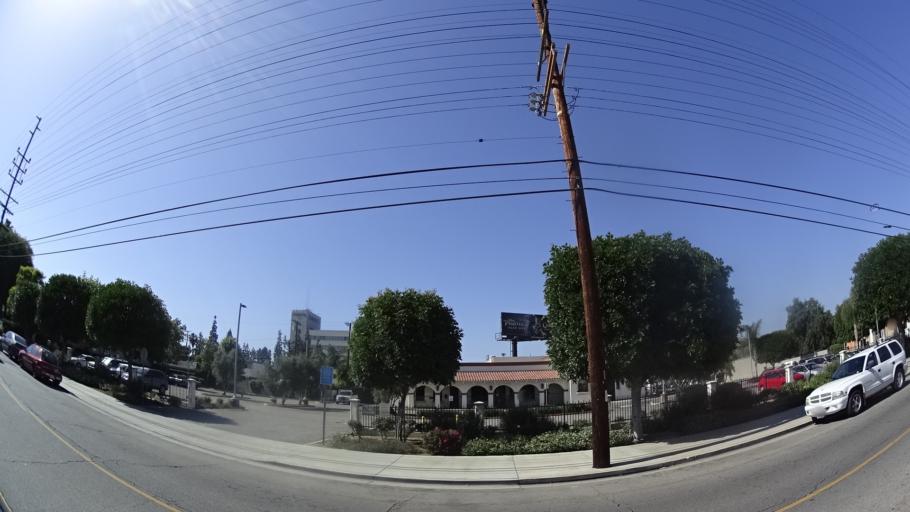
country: US
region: California
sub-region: Los Angeles County
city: Universal City
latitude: 34.1504
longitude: -118.3668
